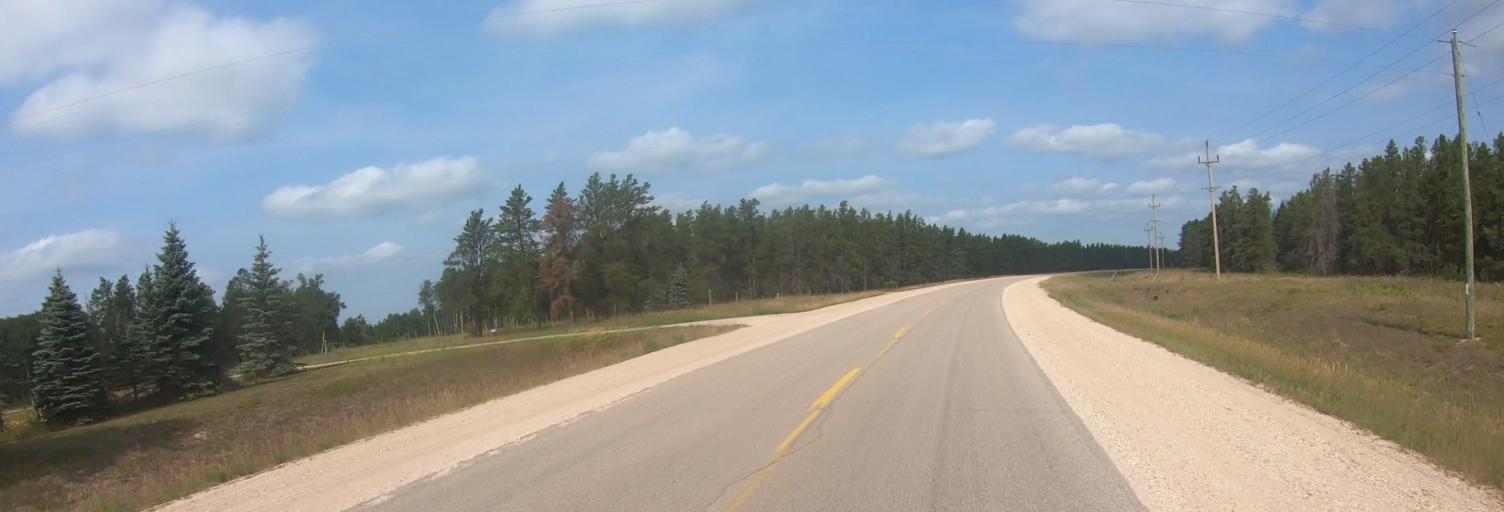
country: CA
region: Manitoba
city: La Broquerie
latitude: 49.2374
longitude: -96.3454
